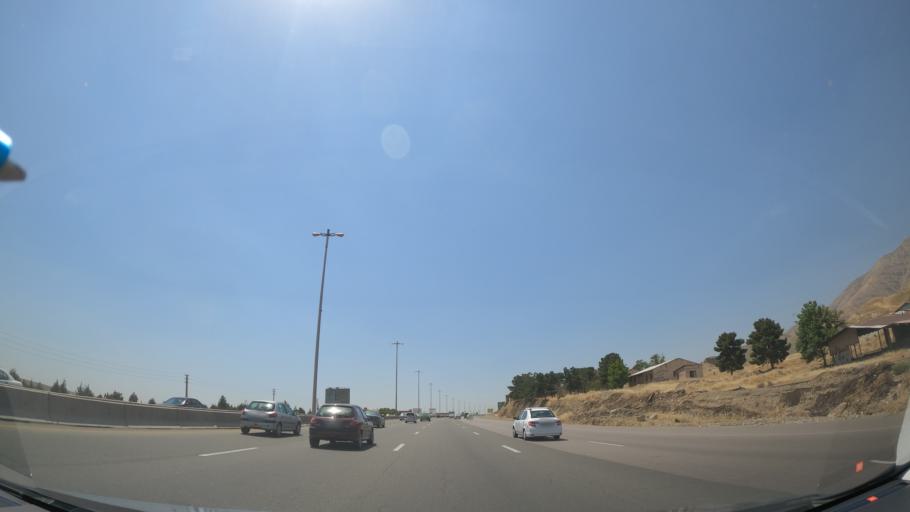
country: IR
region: Tehran
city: Shahr-e Qods
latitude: 35.7445
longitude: 51.0956
